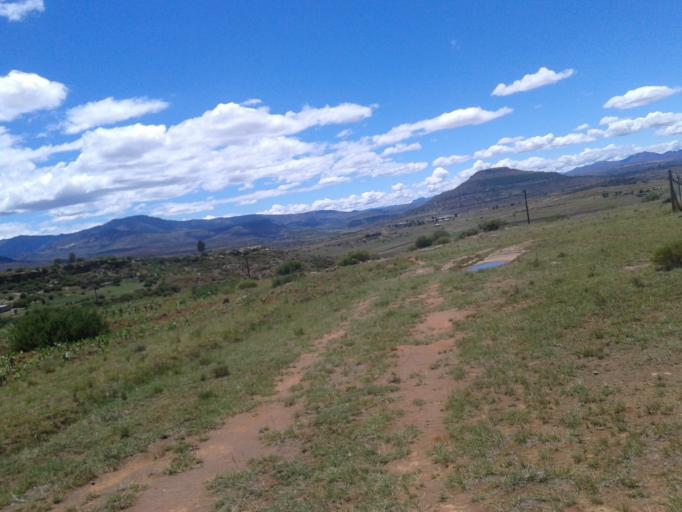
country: LS
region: Quthing
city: Quthing
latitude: -30.3810
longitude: 27.5576
